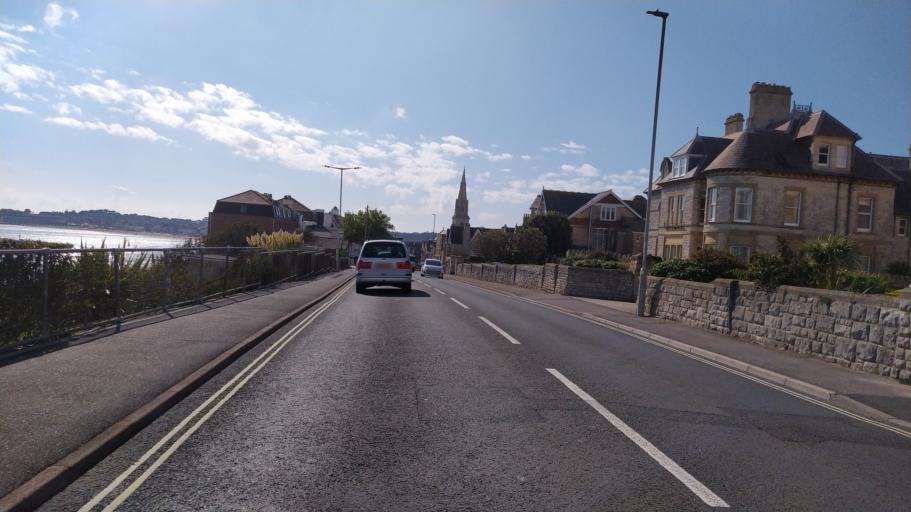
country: GB
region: England
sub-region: Dorset
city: Weymouth
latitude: 50.6212
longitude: -2.4482
